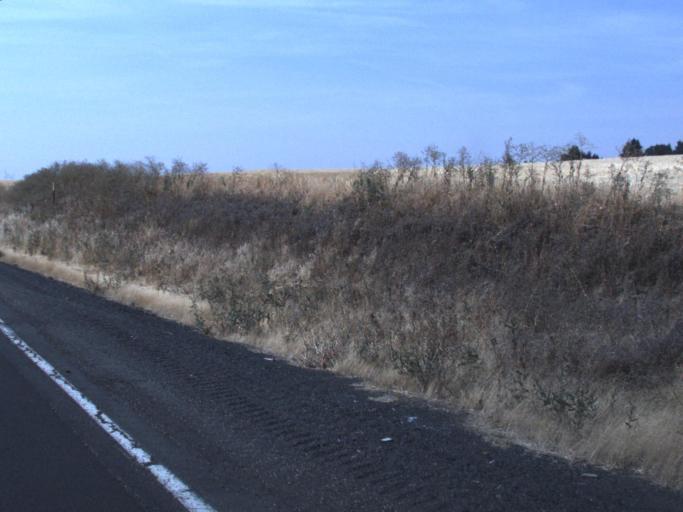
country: US
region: Washington
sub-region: Whitman County
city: Colfax
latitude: 47.1232
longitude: -117.2143
